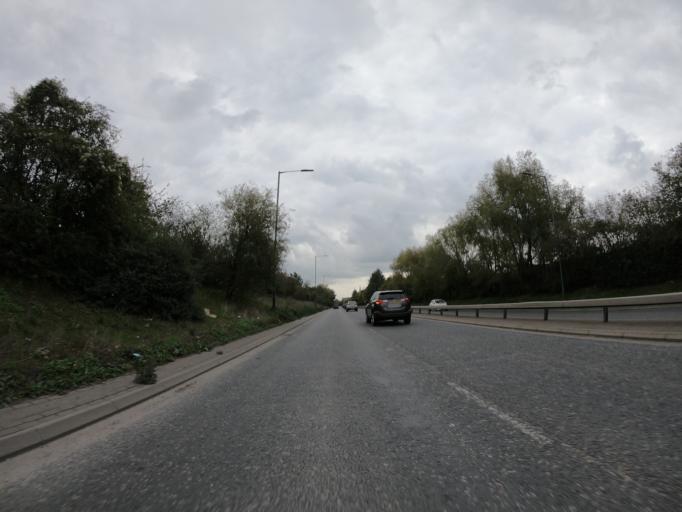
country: GB
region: England
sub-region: Greater London
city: Erith
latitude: 51.4859
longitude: 0.1704
